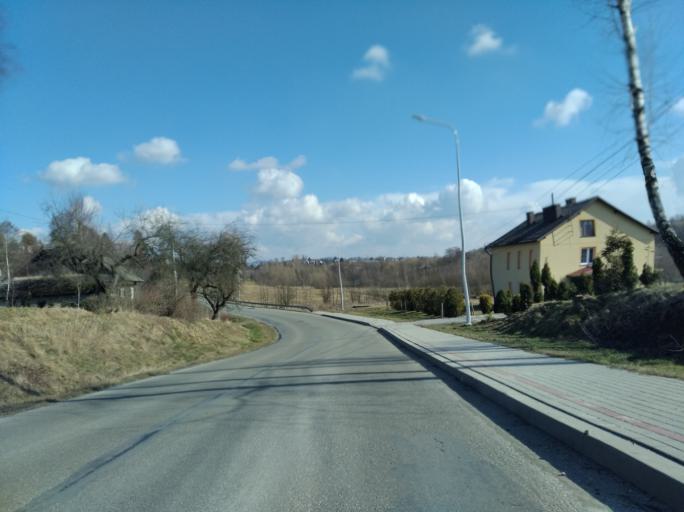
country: PL
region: Subcarpathian Voivodeship
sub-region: Powiat strzyzowski
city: Frysztak
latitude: 49.8442
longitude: 21.5715
